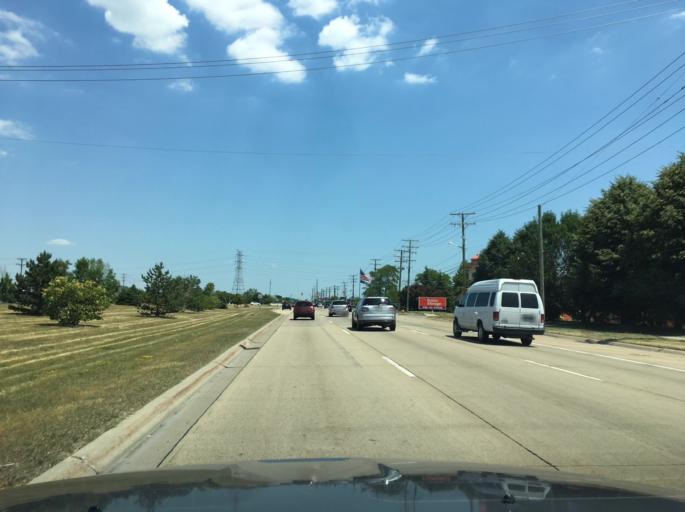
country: US
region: Michigan
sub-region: Macomb County
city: Clinton
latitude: 42.6284
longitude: -82.9230
